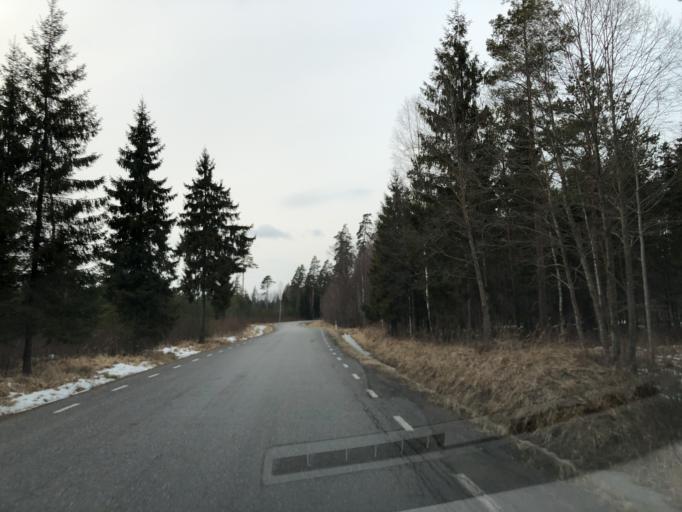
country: EE
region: Paernumaa
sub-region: Vaendra vald (alev)
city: Vandra
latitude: 58.6890
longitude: 24.9821
